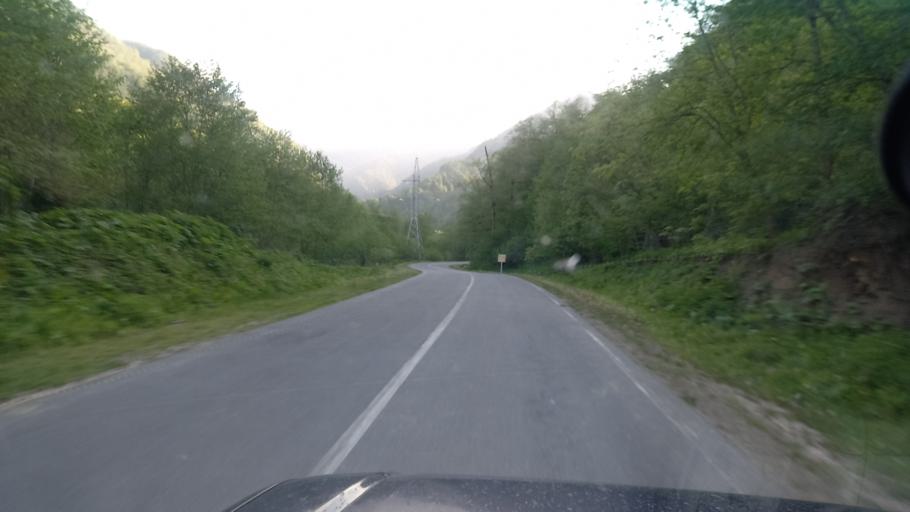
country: RU
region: North Ossetia
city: Tarskoye
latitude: 42.9036
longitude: 44.9542
